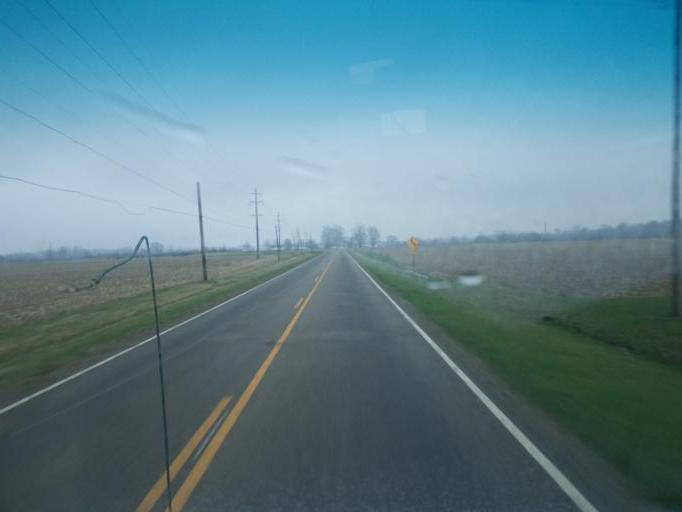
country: US
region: Ohio
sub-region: Defiance County
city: Hicksville
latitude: 41.3410
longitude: -84.7670
